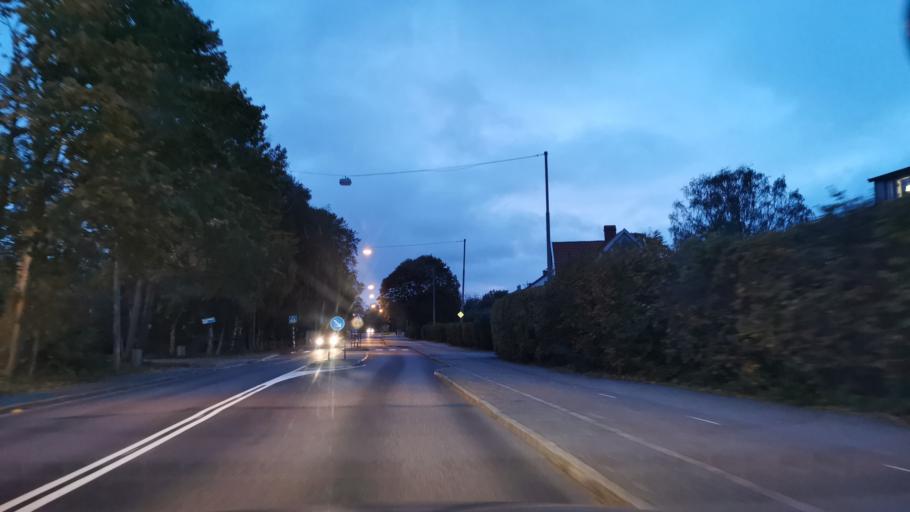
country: SE
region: Vaestra Goetaland
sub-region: Goteborg
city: Eriksbo
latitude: 57.7355
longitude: 12.0498
